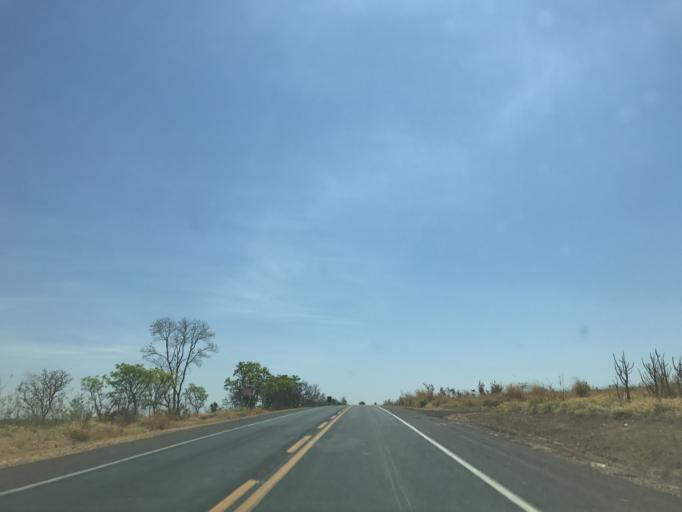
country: BR
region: Minas Gerais
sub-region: Prata
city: Prata
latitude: -19.5160
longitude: -48.8385
